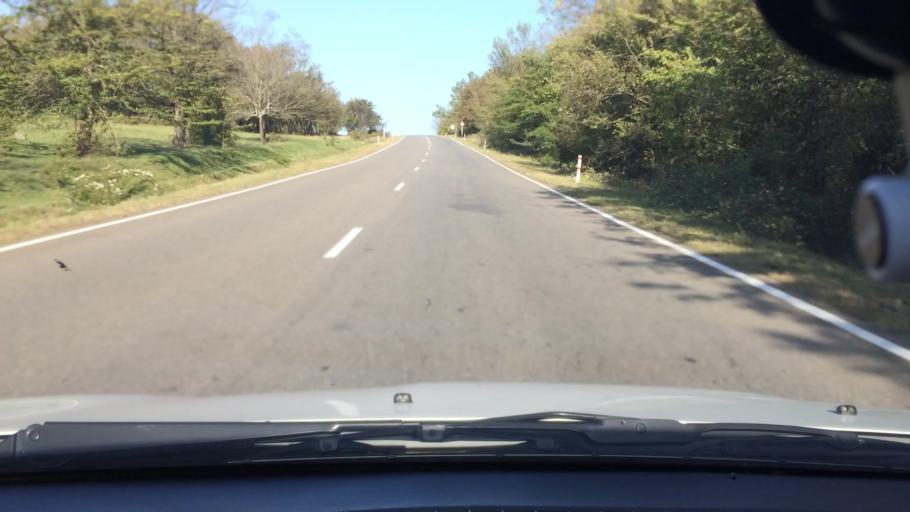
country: GE
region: Imereti
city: Kutaisi
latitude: 42.2505
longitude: 42.7537
